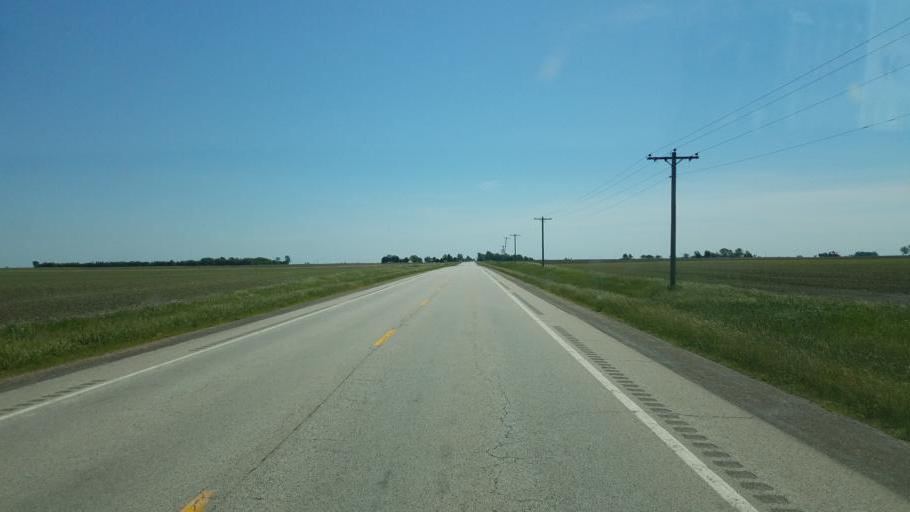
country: US
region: Illinois
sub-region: McLean County
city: Heyworth
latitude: 40.3123
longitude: -88.9327
